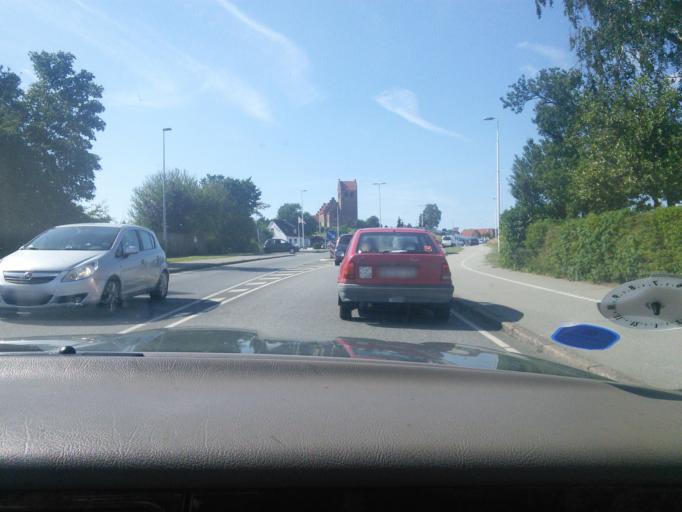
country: DK
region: Capital Region
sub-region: Halsnaes Kommune
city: Frederiksvaerk
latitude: 55.9446
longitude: 12.0507
